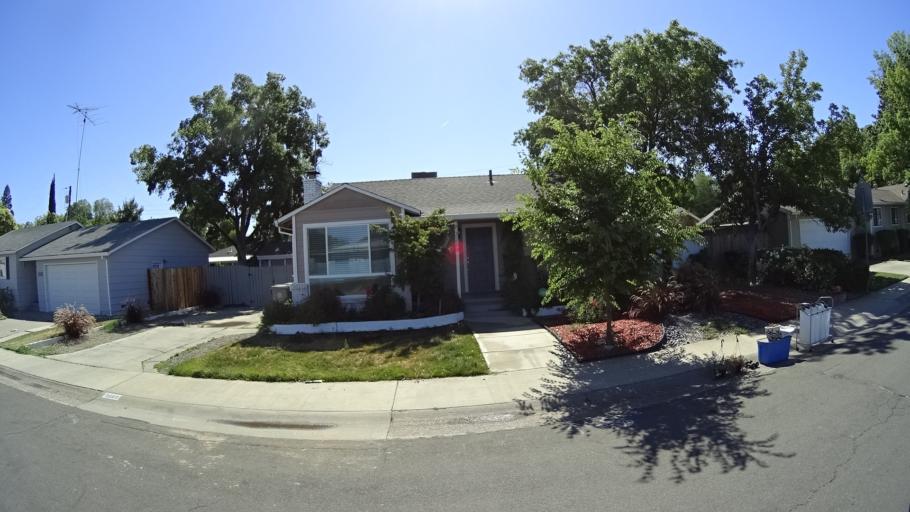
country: US
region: California
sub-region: Sacramento County
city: Parkway
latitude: 38.5453
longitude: -121.4353
